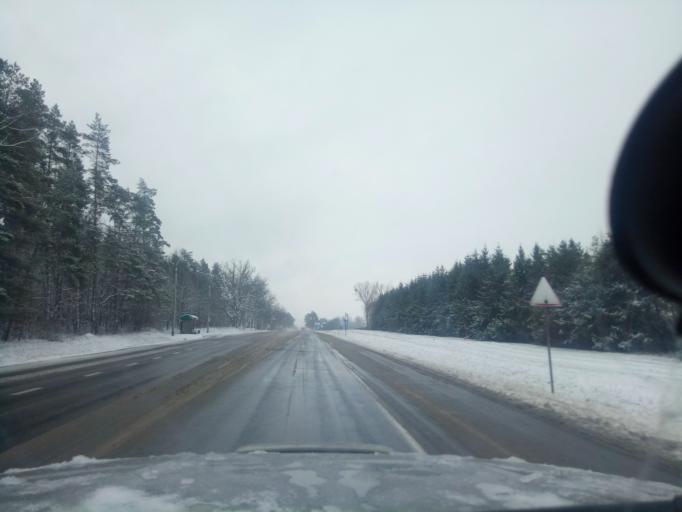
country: BY
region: Minsk
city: Haradzyeya
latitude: 53.2743
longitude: 26.5965
